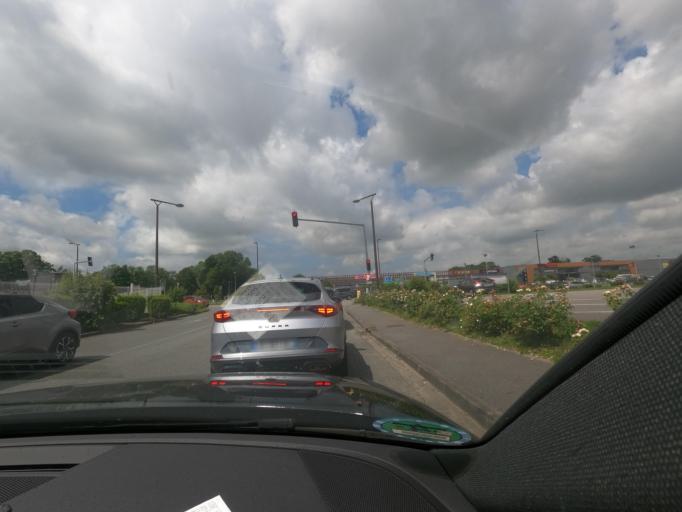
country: FR
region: Haute-Normandie
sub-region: Departement de la Seine-Maritime
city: Sainte-Marie-des-Champs
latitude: 49.6241
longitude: 0.7833
